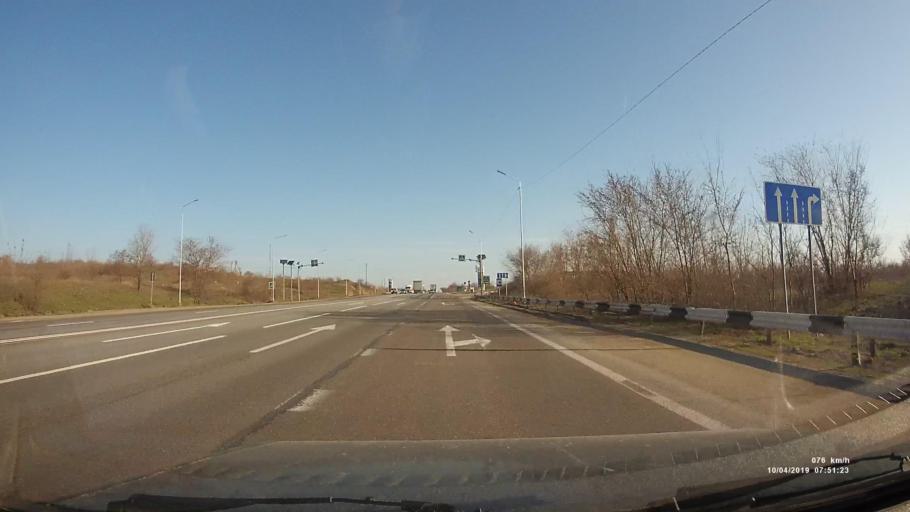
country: RU
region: Rostov
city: Kamensk-Shakhtinskiy
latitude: 48.2733
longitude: 40.2942
